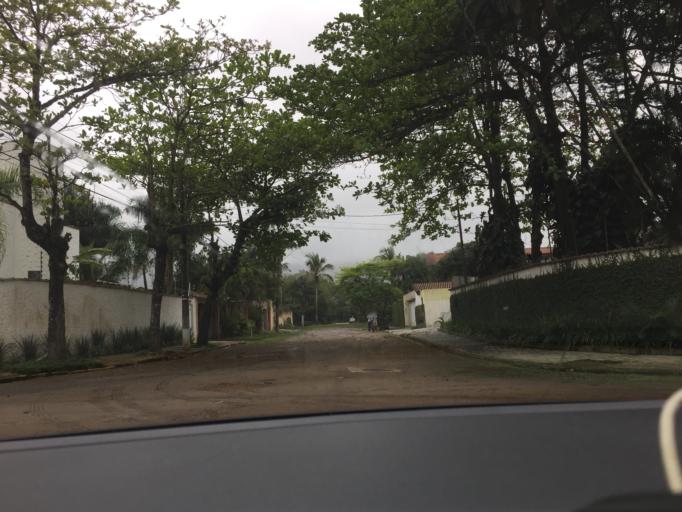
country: BR
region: Sao Paulo
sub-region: Guaruja
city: Guaruja
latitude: -23.9803
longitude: -46.2192
